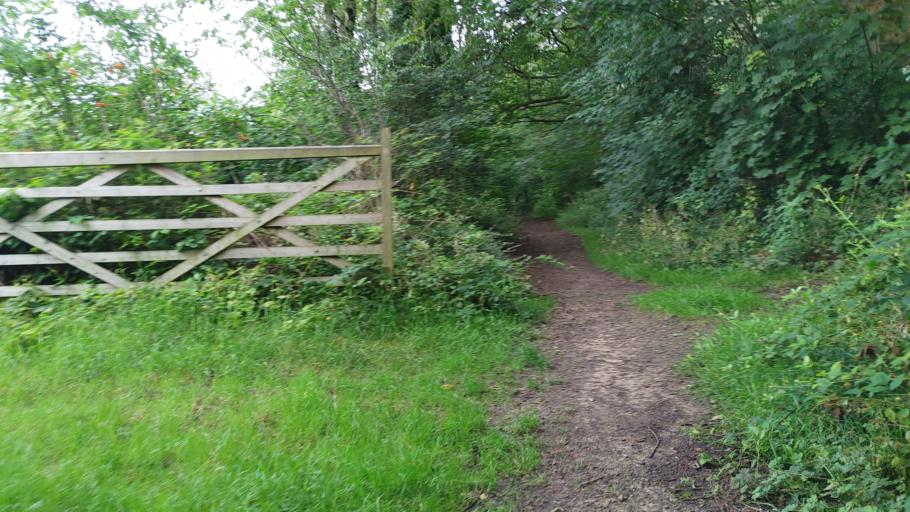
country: GB
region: England
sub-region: Lancashire
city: Chorley
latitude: 53.6325
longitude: -2.6339
